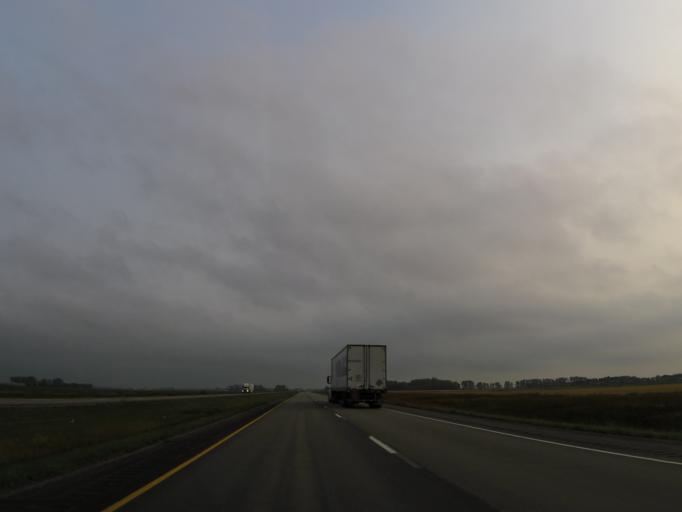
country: US
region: North Dakota
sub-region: Walsh County
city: Grafton
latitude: 48.5471
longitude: -97.1861
